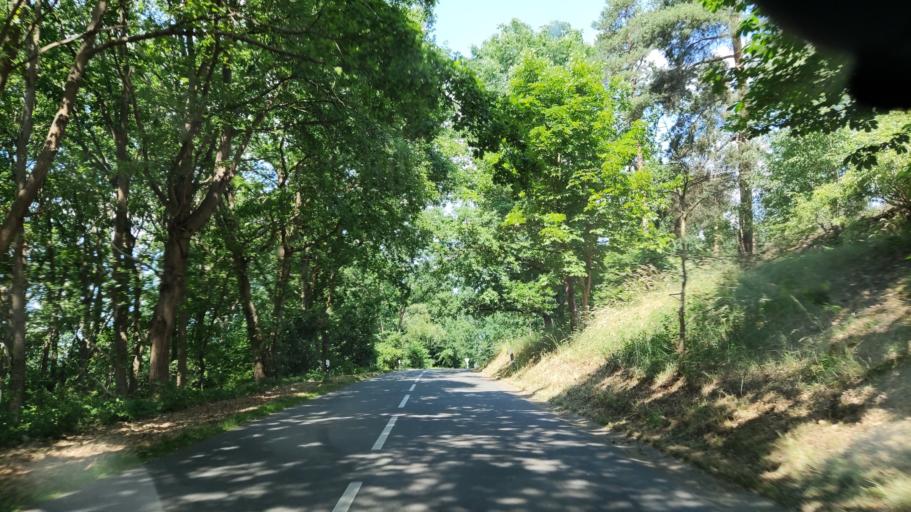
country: DE
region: Lower Saxony
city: Suderburg
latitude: 52.9207
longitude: 10.4601
